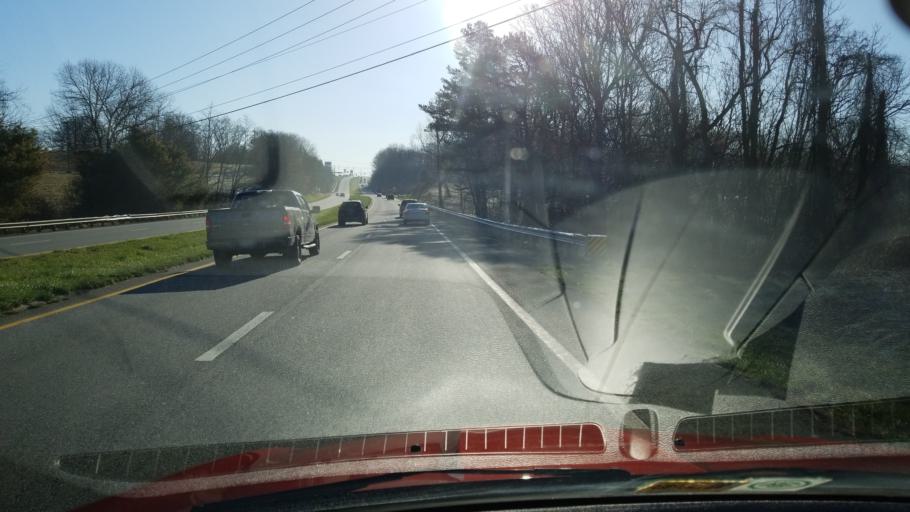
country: US
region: Virginia
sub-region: Franklin County
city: Rocky Mount
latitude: 37.0740
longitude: -79.9082
